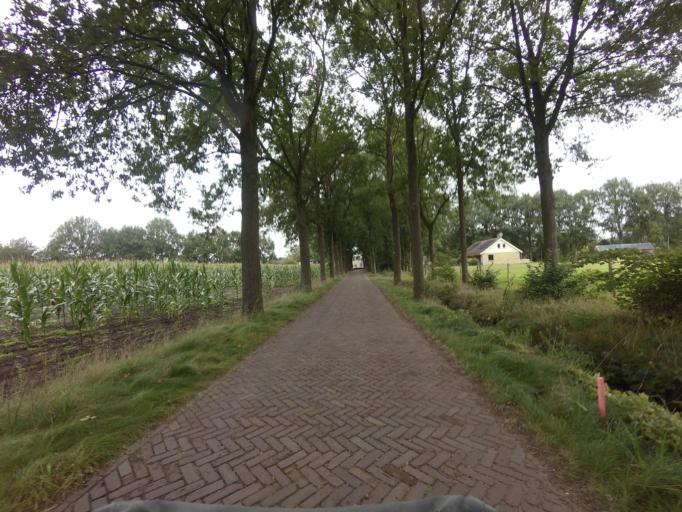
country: DE
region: North Rhine-Westphalia
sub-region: Regierungsbezirk Munster
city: Gronau
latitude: 52.2279
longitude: 7.0313
